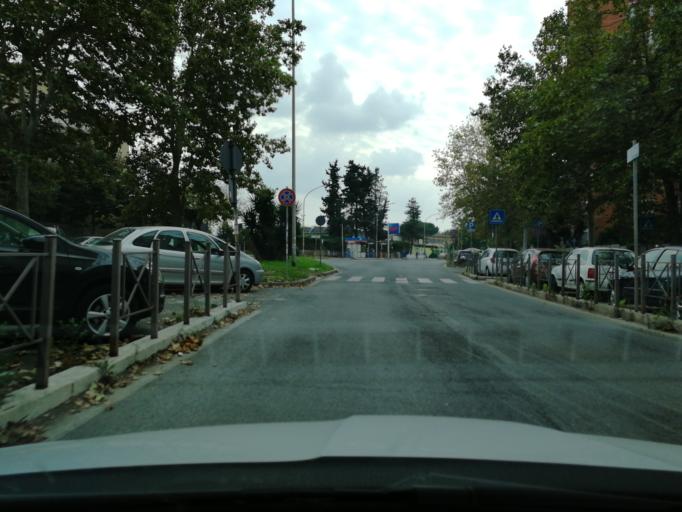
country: IT
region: Latium
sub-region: Citta metropolitana di Roma Capitale
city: Rome
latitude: 41.8567
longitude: 12.5535
